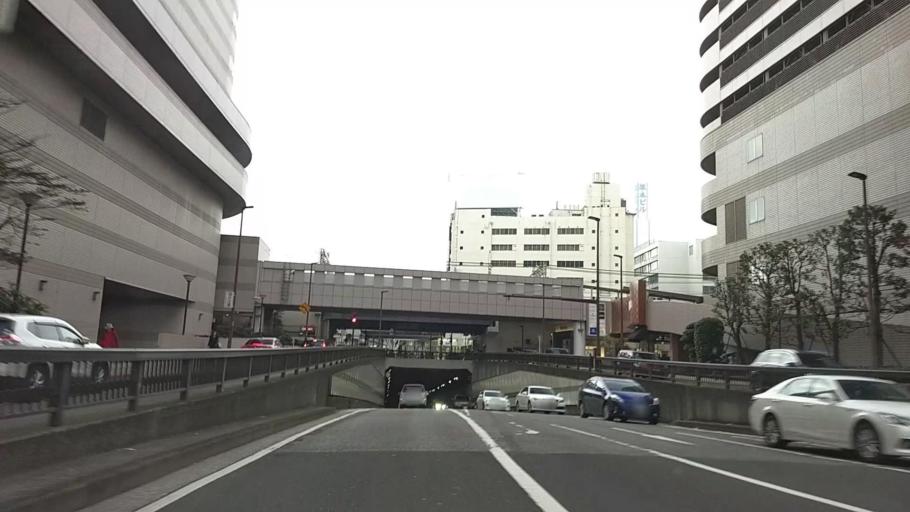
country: JP
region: Chiba
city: Chiba
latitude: 35.6106
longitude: 140.1144
